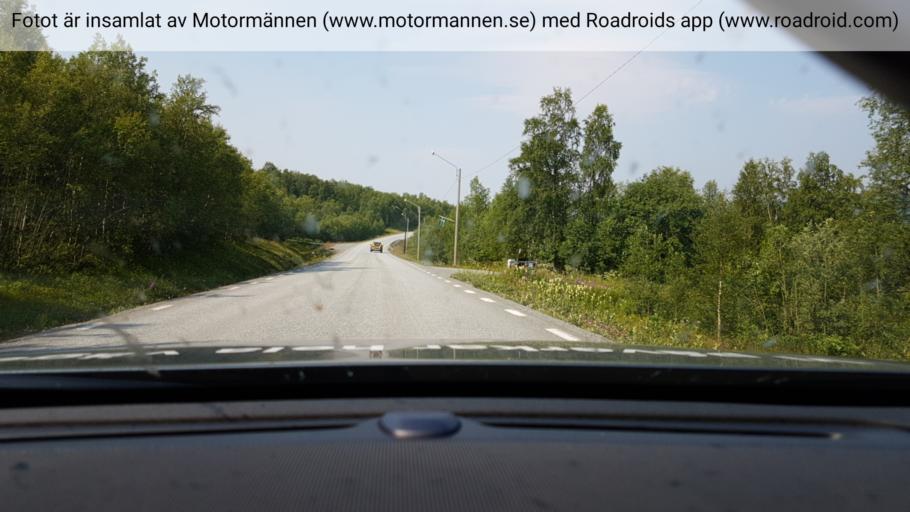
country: NO
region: Nordland
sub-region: Rana
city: Mo i Rana
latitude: 65.7350
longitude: 15.1384
